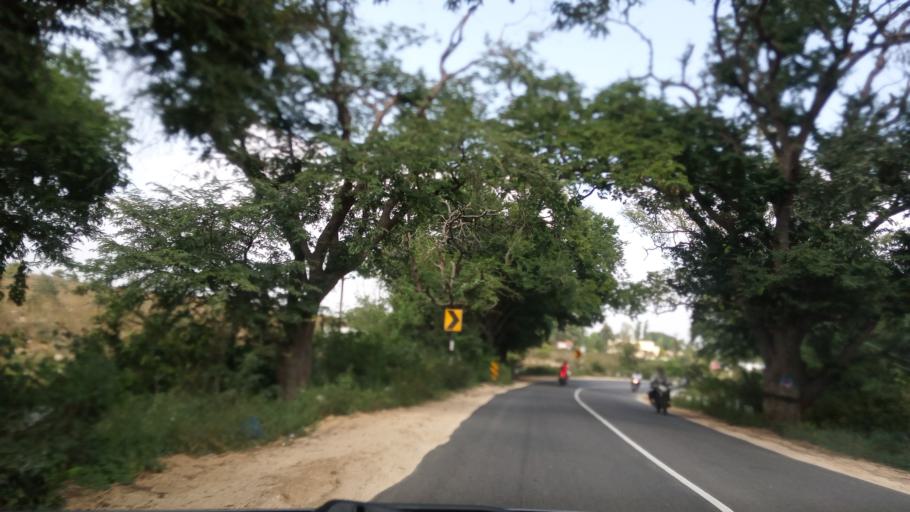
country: IN
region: Andhra Pradesh
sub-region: Chittoor
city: Madanapalle
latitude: 13.5990
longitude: 78.5301
